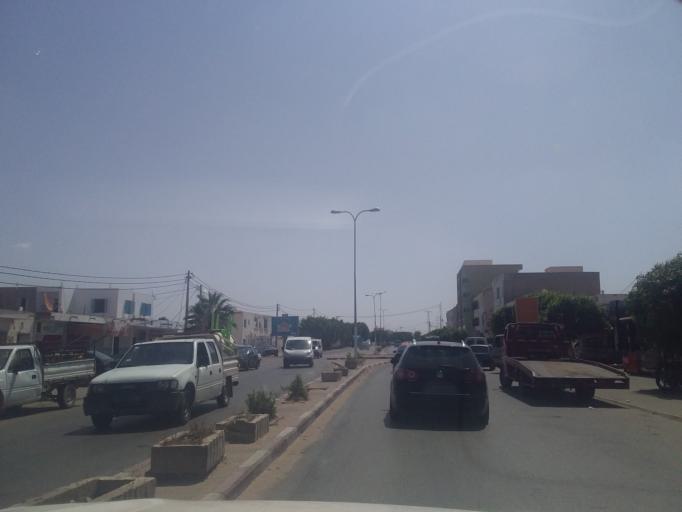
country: TN
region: Qabis
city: Matmata
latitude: 33.6136
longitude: 10.2918
